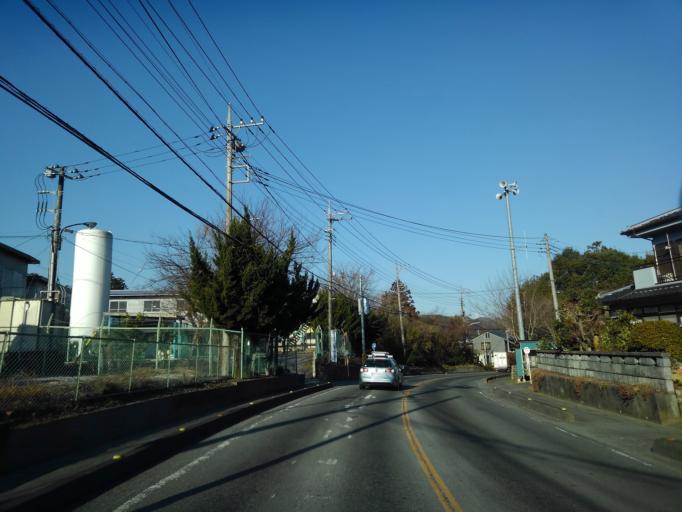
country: JP
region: Saitama
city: Hanno
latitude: 35.8346
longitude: 139.3146
